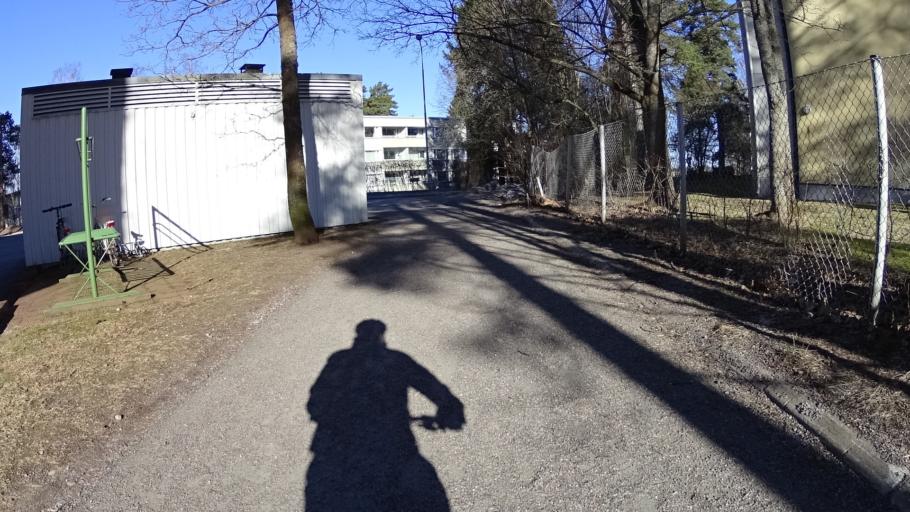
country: FI
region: Uusimaa
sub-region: Helsinki
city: Kauniainen
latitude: 60.2319
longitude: 24.7389
